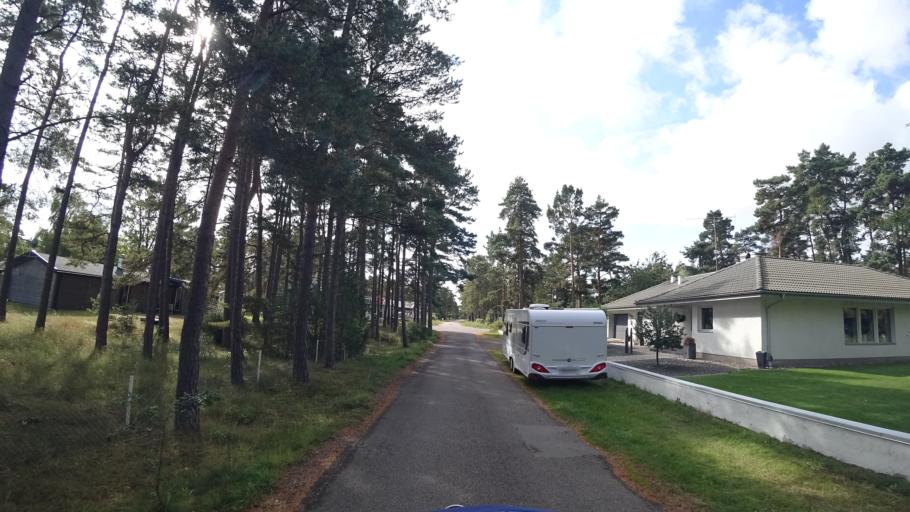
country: SE
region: Skane
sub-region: Kristianstads Kommun
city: Ahus
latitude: 55.9385
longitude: 14.3000
